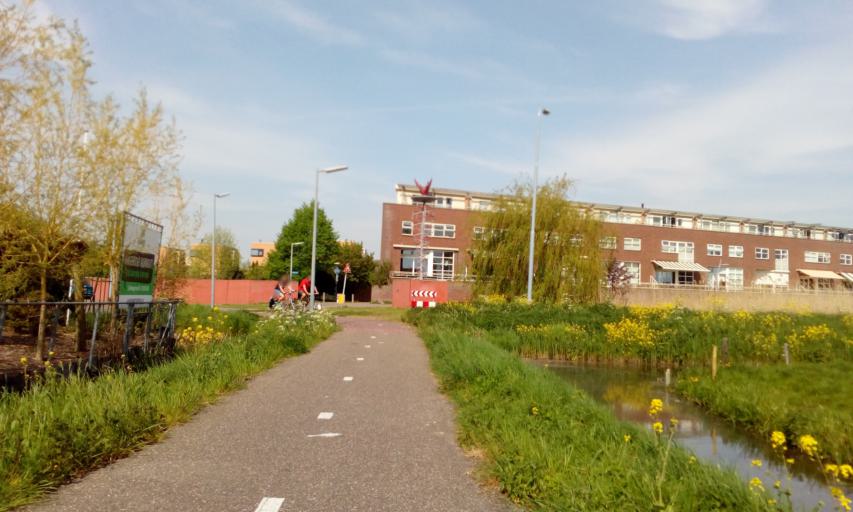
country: NL
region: South Holland
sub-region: Gemeente Lisse
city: Lisse
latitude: 52.2534
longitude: 4.5784
